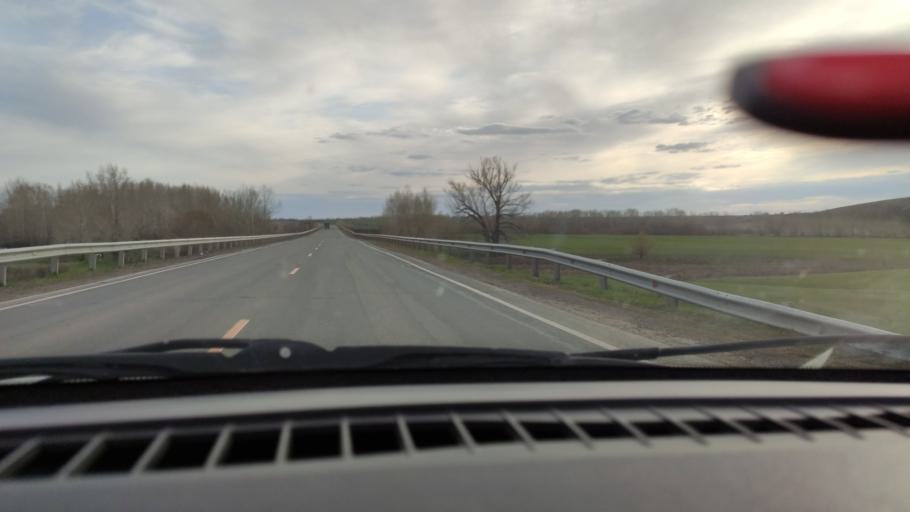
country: RU
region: Orenburg
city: Sakmara
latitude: 52.1989
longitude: 55.3115
